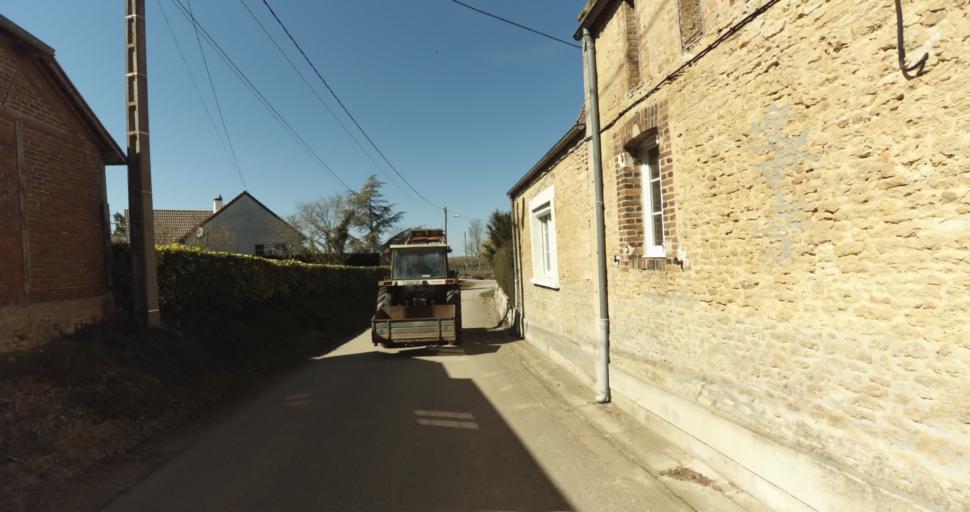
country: FR
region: Lower Normandy
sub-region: Departement du Calvados
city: Saint-Pierre-sur-Dives
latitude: 49.0364
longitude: -0.0057
